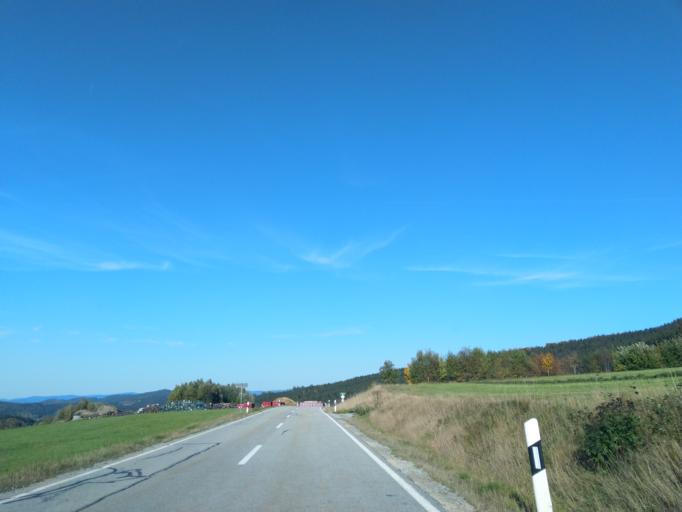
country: DE
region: Bavaria
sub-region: Lower Bavaria
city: Achslach
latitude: 48.9408
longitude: 12.9223
